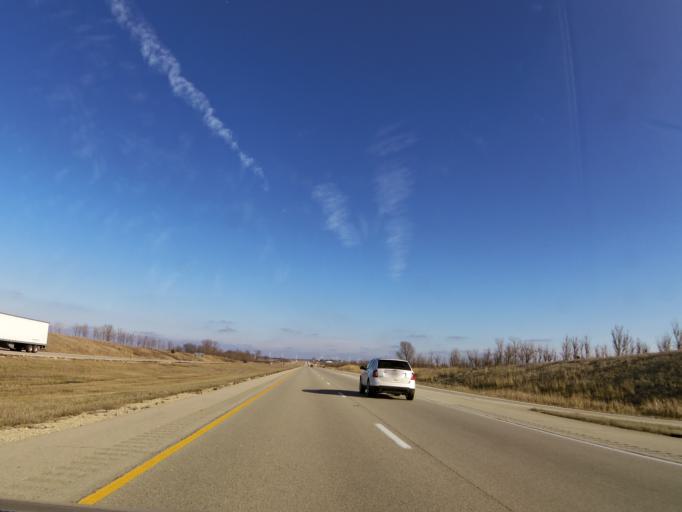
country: US
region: Illinois
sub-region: LaSalle County
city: Earlville
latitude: 41.7007
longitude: -89.0282
